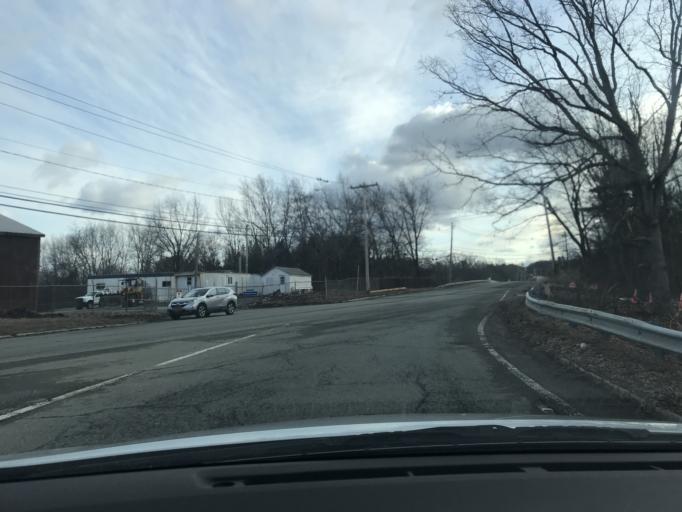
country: US
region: Massachusetts
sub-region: Middlesex County
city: Littleton Common
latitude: 42.5243
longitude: -71.5129
